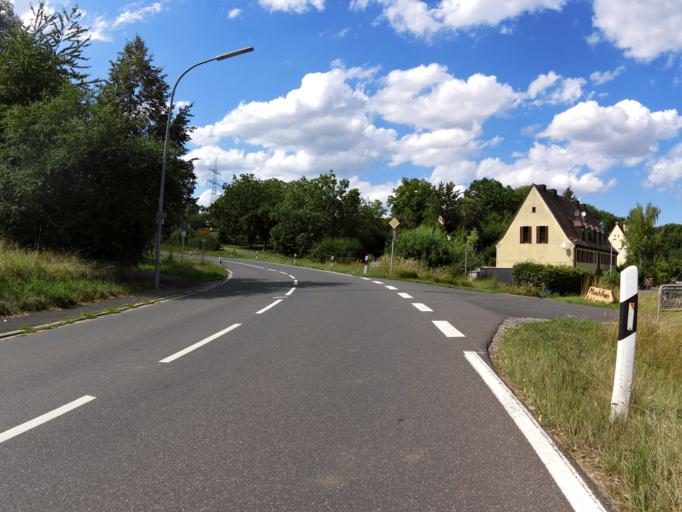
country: DE
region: Bavaria
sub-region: Regierungsbezirk Unterfranken
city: Bergrheinfeld
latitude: 49.9782
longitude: 10.1737
